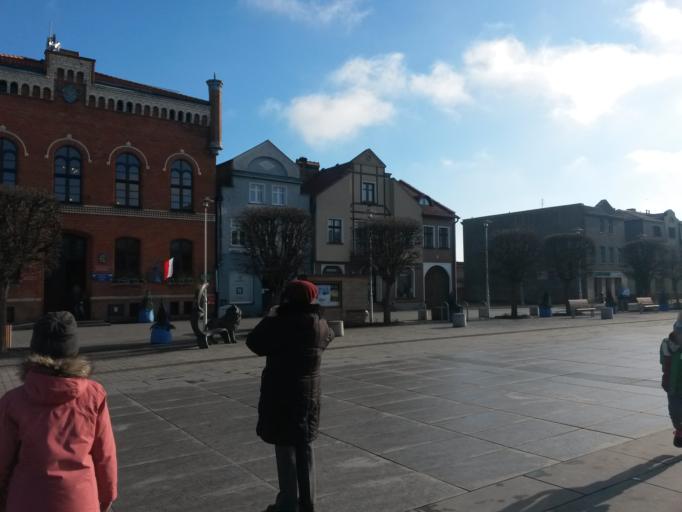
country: PL
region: Pomeranian Voivodeship
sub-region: Powiat pucki
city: Puck
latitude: 54.7206
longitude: 18.4113
